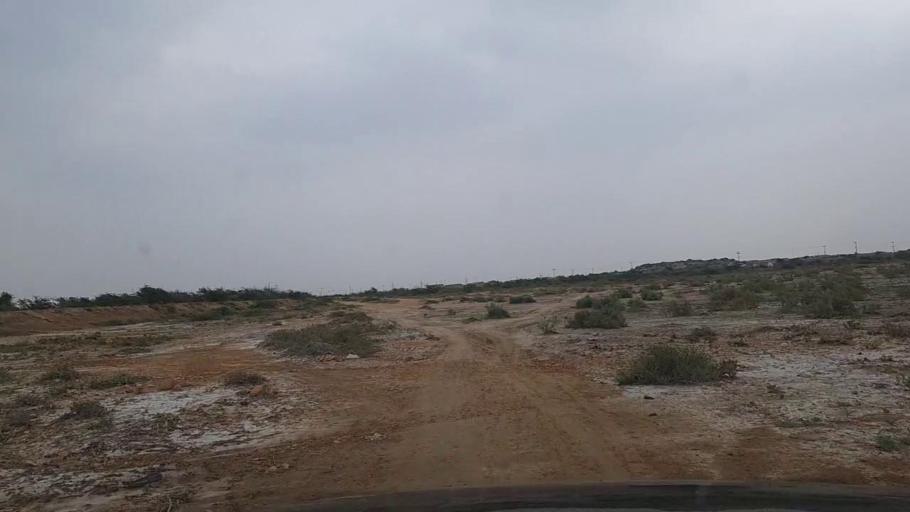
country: PK
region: Sindh
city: Thatta
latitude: 24.8175
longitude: 67.8311
